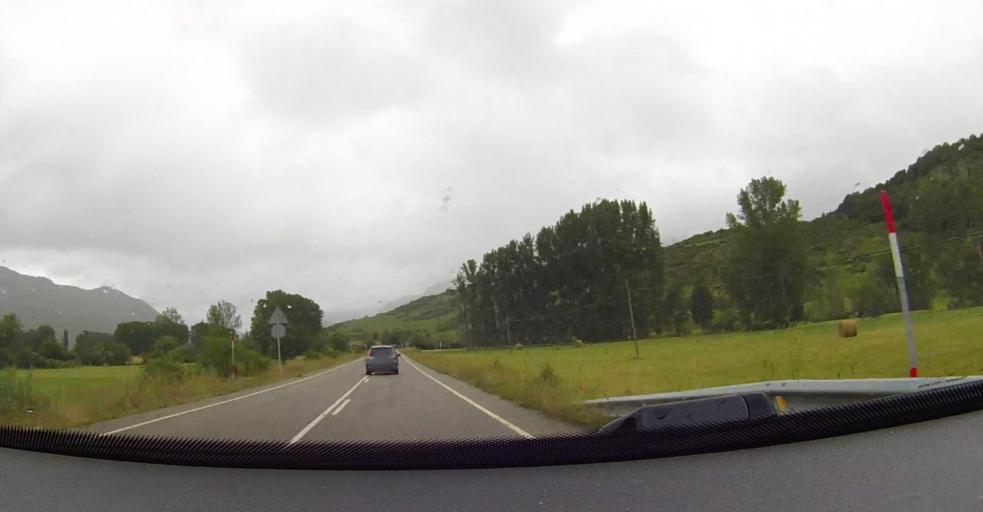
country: ES
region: Castille and Leon
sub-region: Provincia de Leon
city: Acebedo
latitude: 43.0472
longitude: -5.1277
